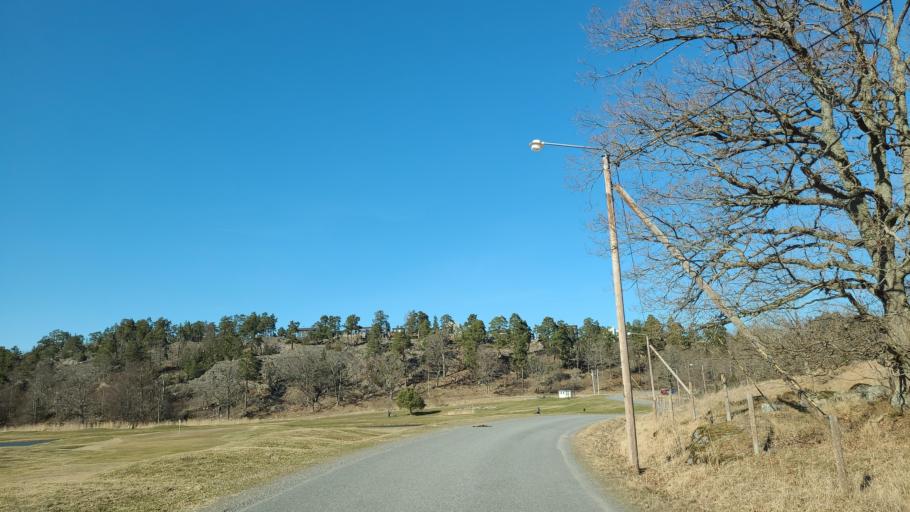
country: SE
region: Stockholm
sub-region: Varmdo Kommun
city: Hemmesta
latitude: 59.2759
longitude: 18.5475
